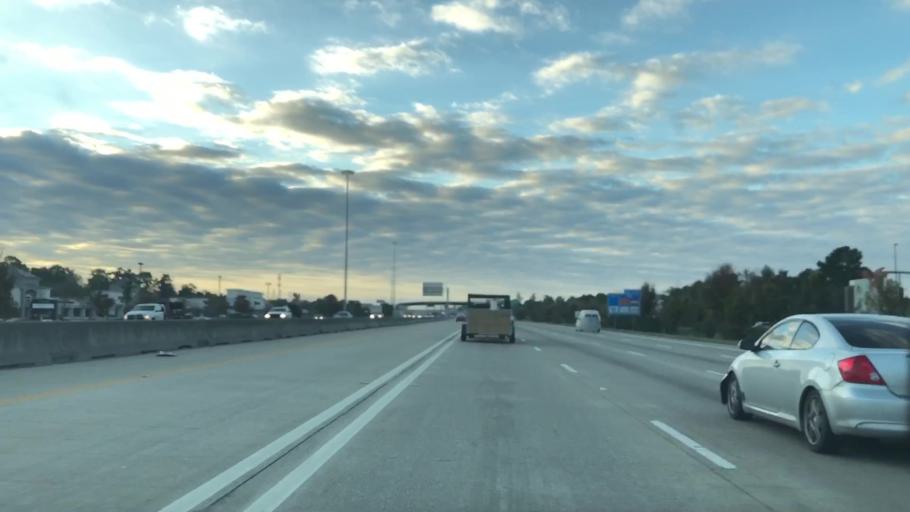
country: US
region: Texas
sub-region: Montgomery County
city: Oak Ridge North
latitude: 30.1641
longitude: -95.4504
